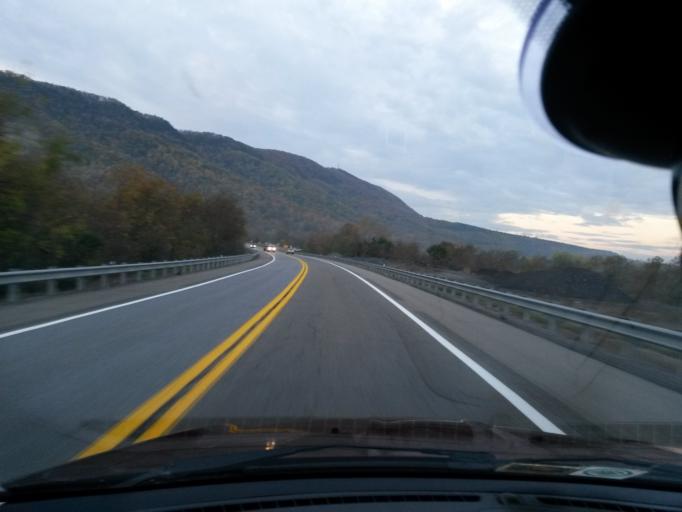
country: US
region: Virginia
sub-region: Alleghany County
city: Clifton Forge
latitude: 37.6523
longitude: -79.8122
